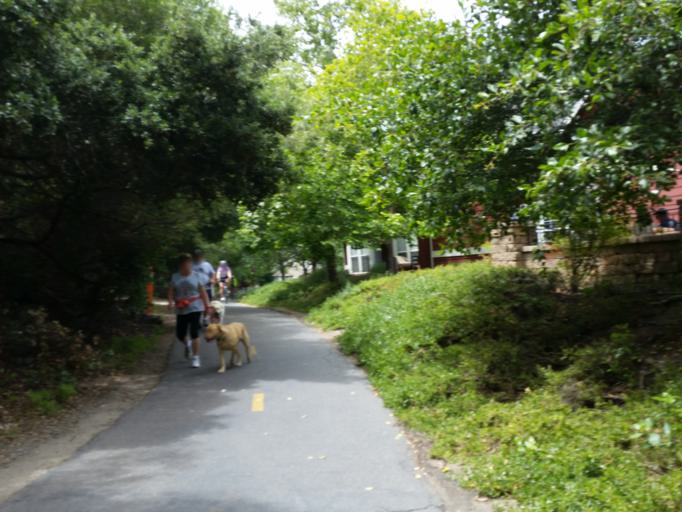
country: US
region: California
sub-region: San Luis Obispo County
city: Avila Beach
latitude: 35.1889
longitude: -120.7200
